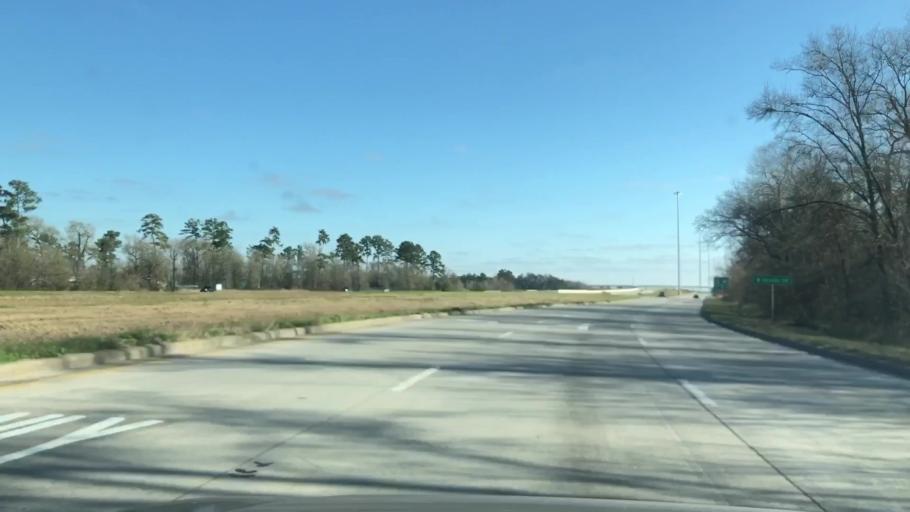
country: US
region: Texas
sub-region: Harris County
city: Cloverleaf
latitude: 29.8249
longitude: -95.1919
